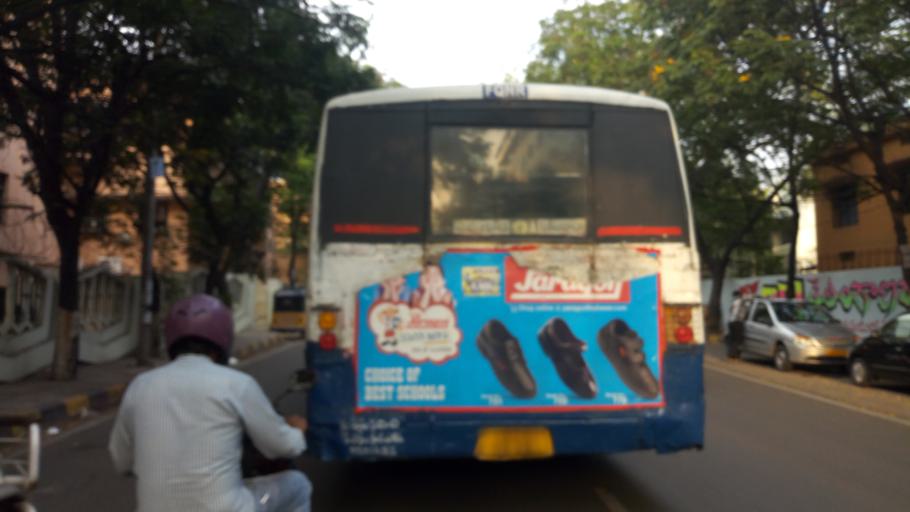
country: IN
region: Telangana
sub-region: Hyderabad
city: Hyderabad
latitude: 17.3982
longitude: 78.4730
